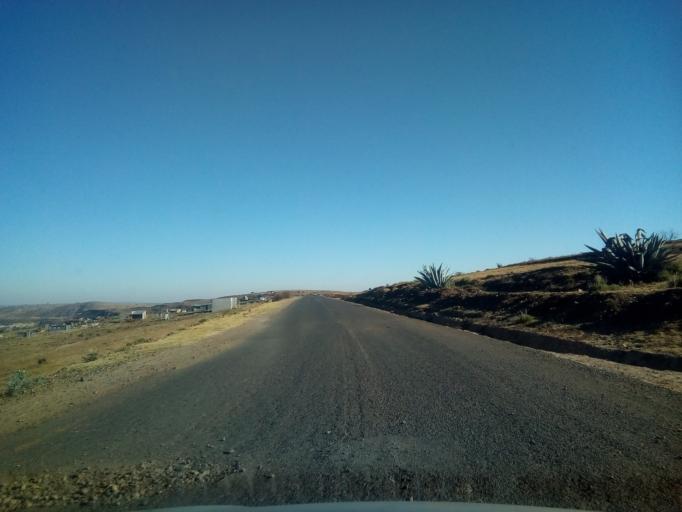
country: LS
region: Berea
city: Teyateyaneng
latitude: -29.2564
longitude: 27.8021
